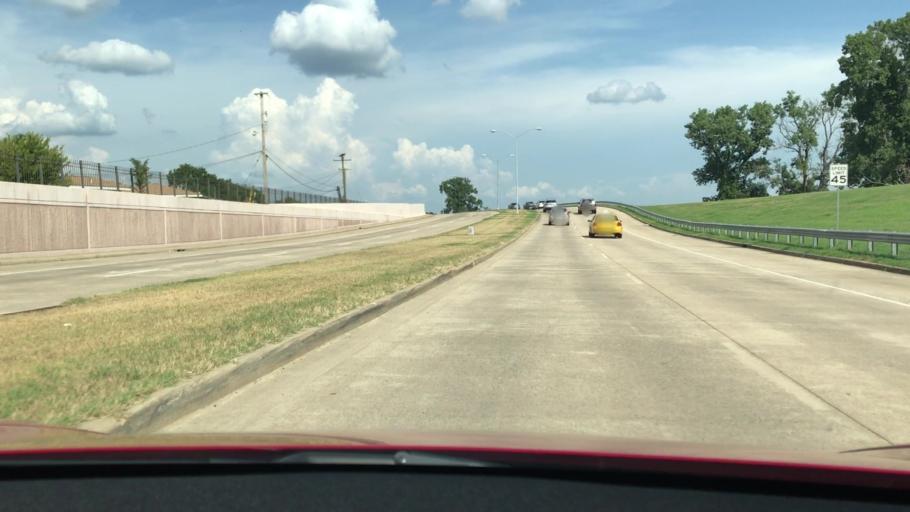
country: US
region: Louisiana
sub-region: Bossier Parish
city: Bossier City
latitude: 32.5111
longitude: -93.7229
